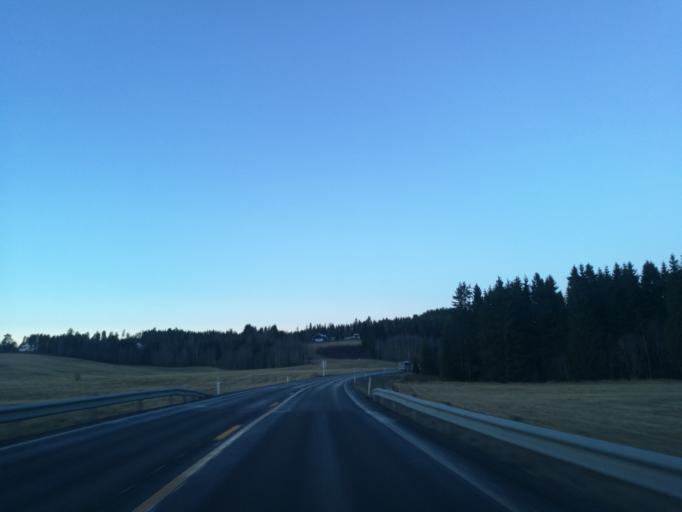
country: NO
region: Hedmark
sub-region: Eidskog
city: Skotterud
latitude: 59.9880
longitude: 12.1064
